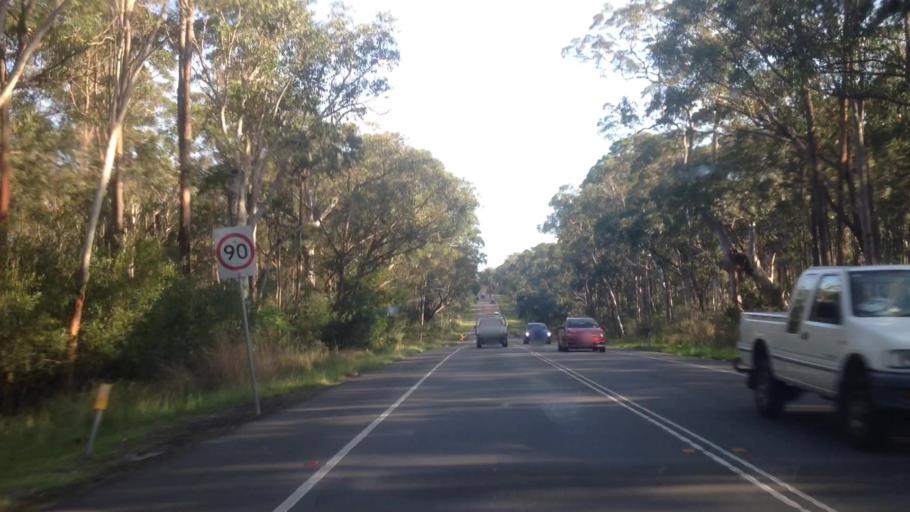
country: AU
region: New South Wales
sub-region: Lake Macquarie Shire
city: Dora Creek
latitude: -33.1379
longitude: 151.4774
